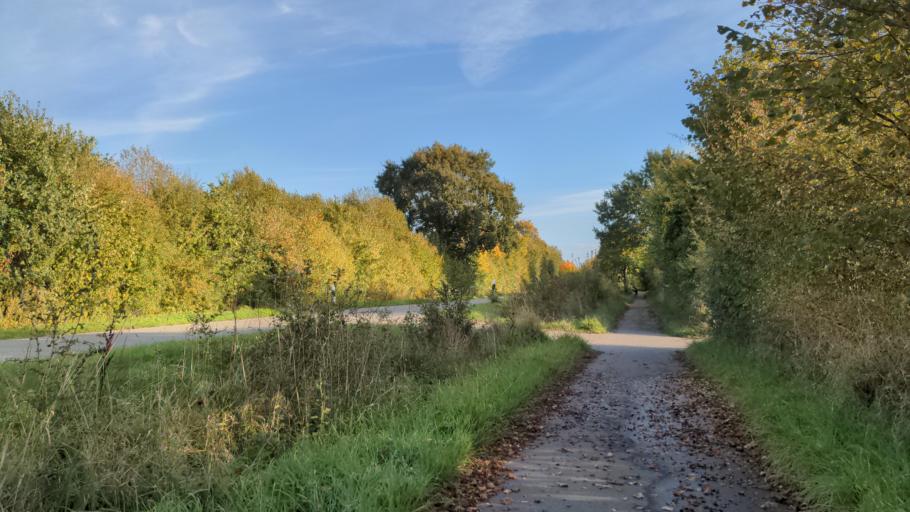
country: DE
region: Schleswig-Holstein
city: Kabelhorst
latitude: 54.2107
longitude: 10.9199
